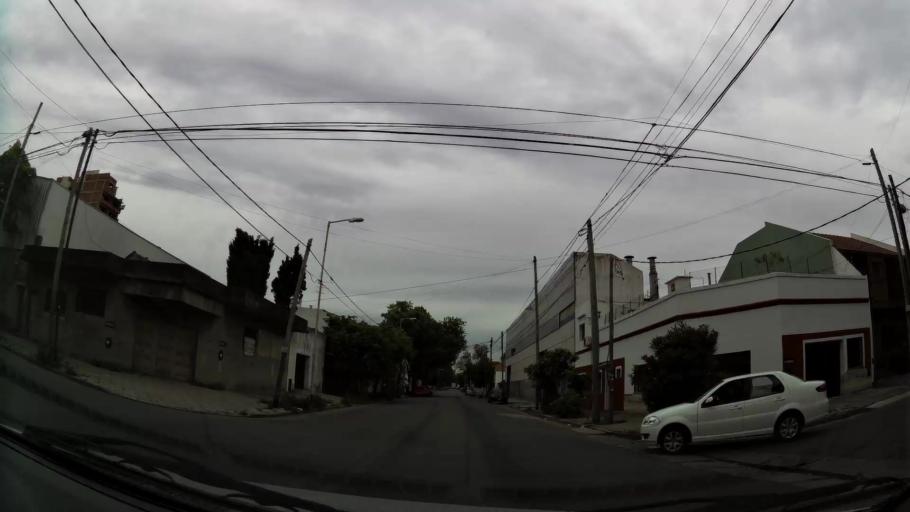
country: AR
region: Buenos Aires
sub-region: Partido de Avellaneda
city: Avellaneda
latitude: -34.6739
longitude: -58.3846
